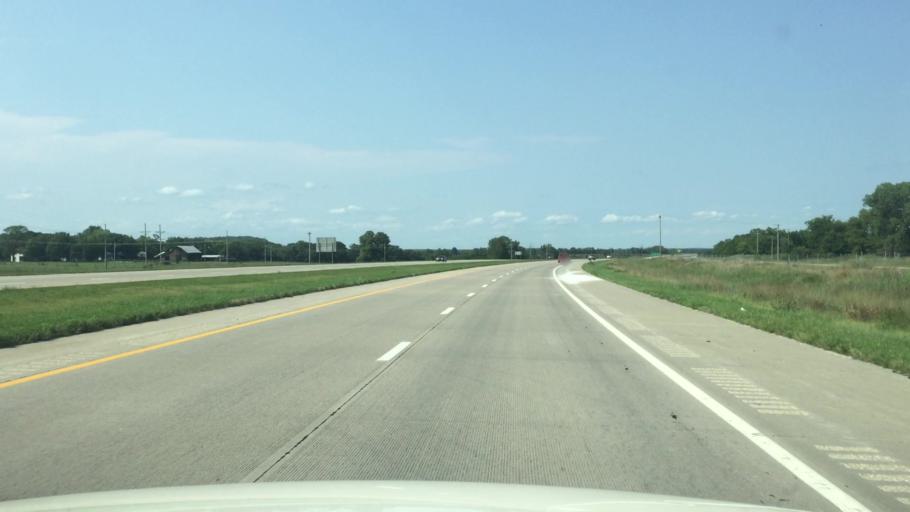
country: US
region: Kansas
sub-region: Linn County
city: Pleasanton
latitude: 38.1932
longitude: -94.7050
